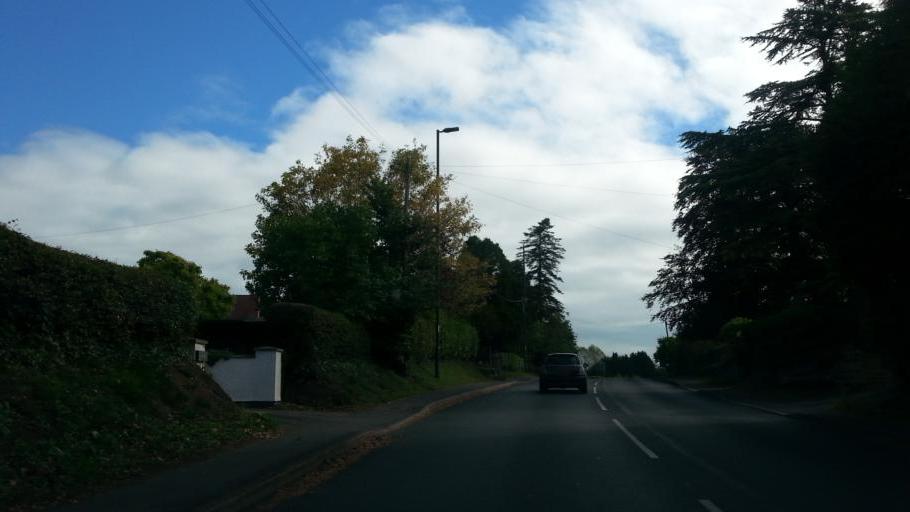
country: GB
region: England
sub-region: Herefordshire
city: Ross on Wye
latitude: 51.9138
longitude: -2.5671
